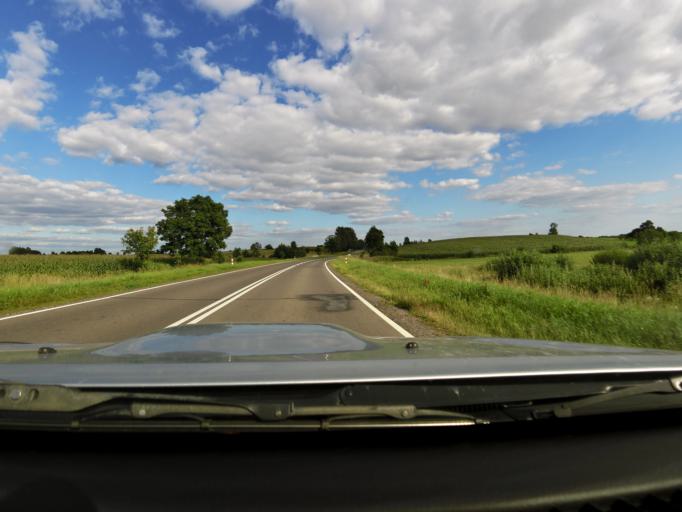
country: PL
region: Podlasie
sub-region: Powiat suwalski
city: Raczki
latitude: 53.8577
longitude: 22.7591
